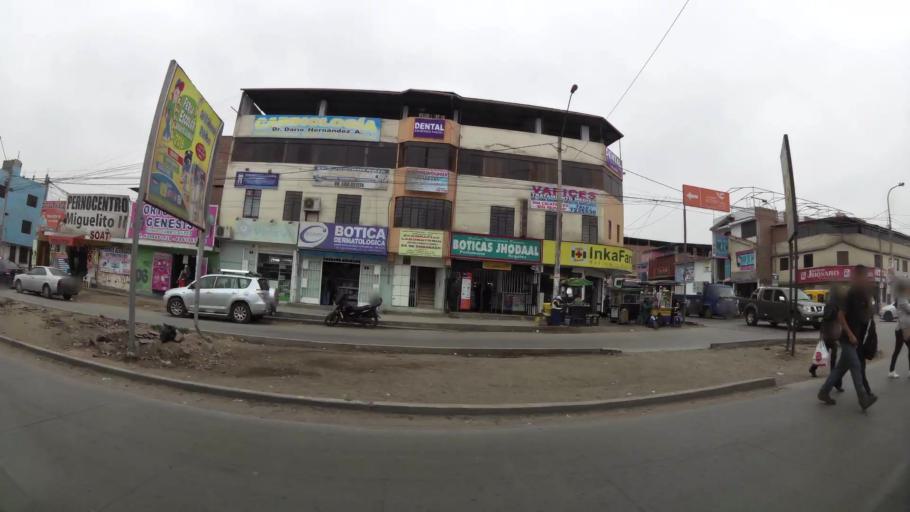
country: PE
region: Lima
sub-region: Lima
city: Surco
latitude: -12.1953
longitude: -76.9592
